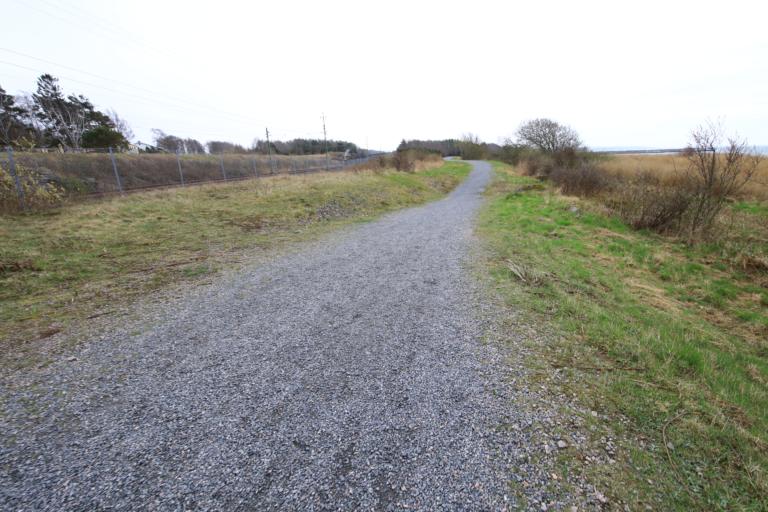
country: SE
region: Halland
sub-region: Kungsbacka Kommun
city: Frillesas
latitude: 57.3026
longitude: 12.1683
